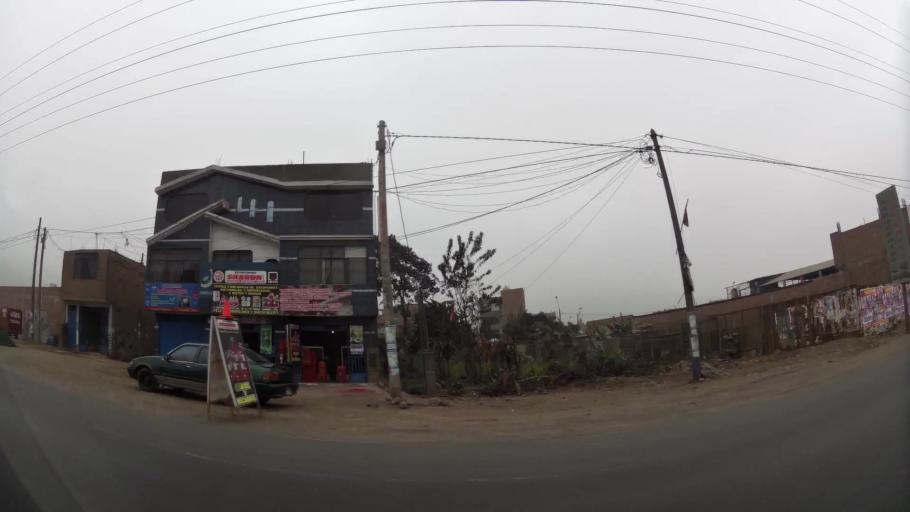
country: PE
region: Lima
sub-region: Lima
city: Santa Maria
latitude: -12.0115
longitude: -76.8760
